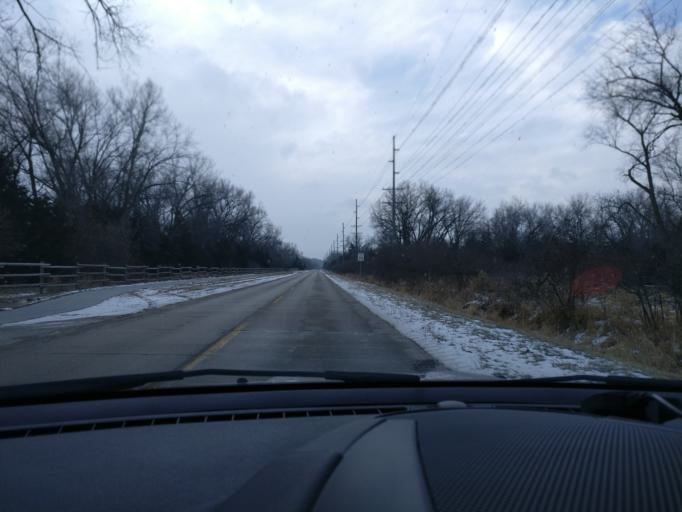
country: US
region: Nebraska
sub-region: Dodge County
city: Fremont
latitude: 41.4298
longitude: -96.5215
